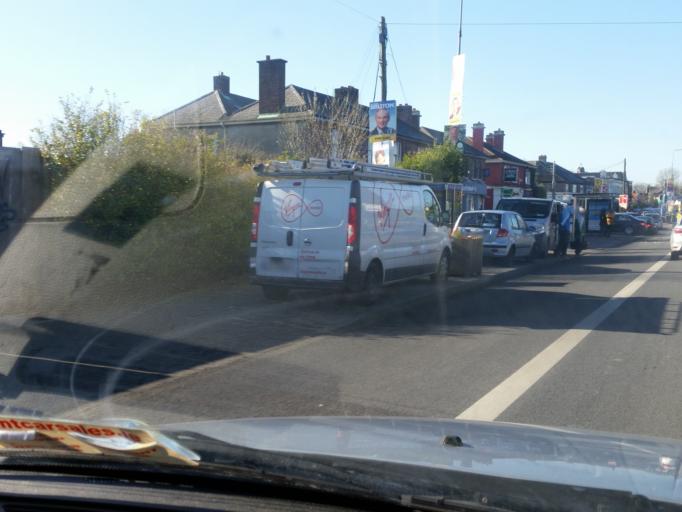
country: IE
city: Killester
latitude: 53.3712
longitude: -6.2038
